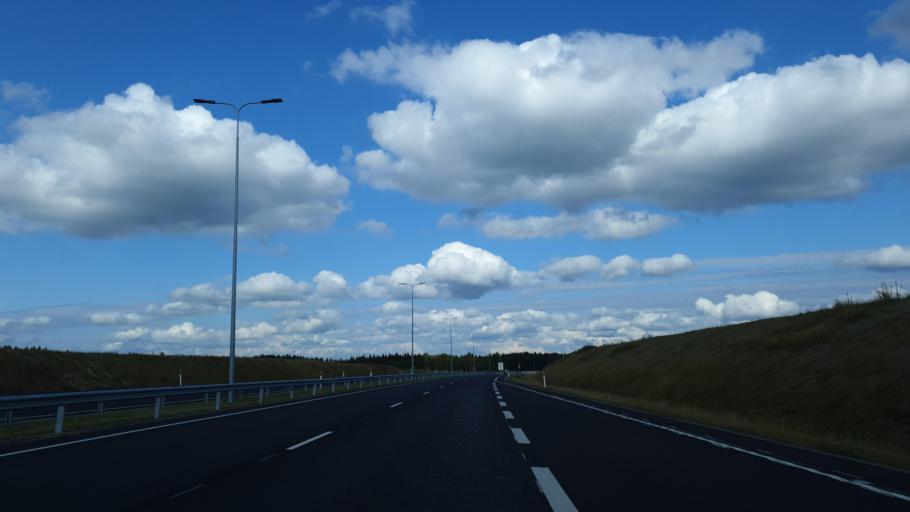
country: FI
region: Southern Savonia
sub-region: Mikkeli
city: Mikkeli
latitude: 61.7166
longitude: 27.3421
